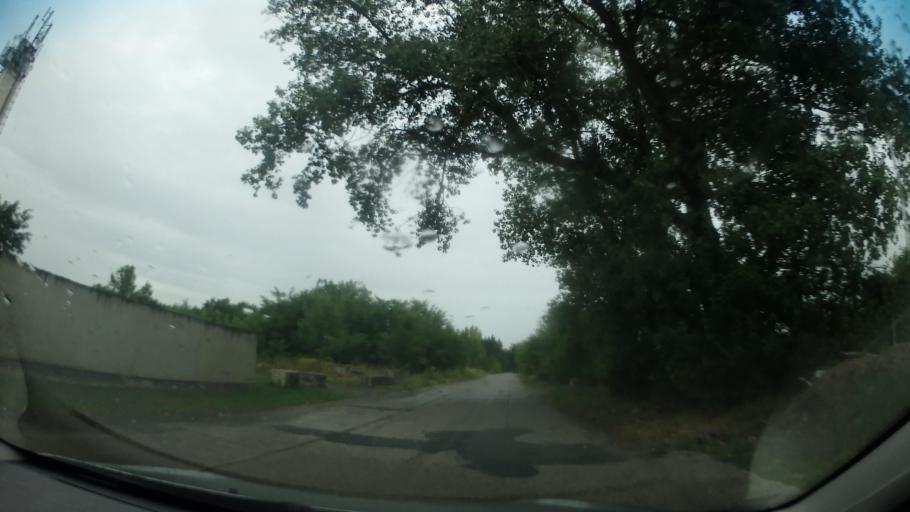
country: CZ
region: Central Bohemia
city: Milovice
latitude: 50.2403
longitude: 14.9150
